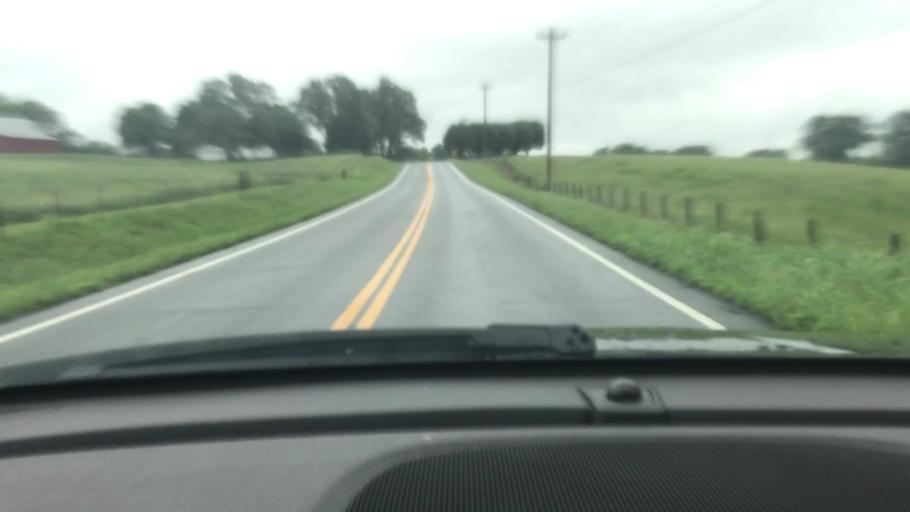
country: US
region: Tennessee
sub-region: Dickson County
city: Charlotte
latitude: 36.2079
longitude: -87.2827
